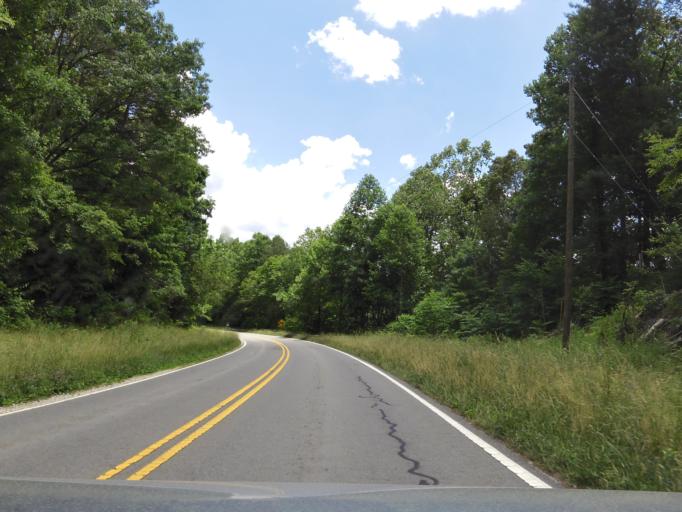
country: US
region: North Carolina
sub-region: Graham County
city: Robbinsville
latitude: 35.3681
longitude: -83.8416
